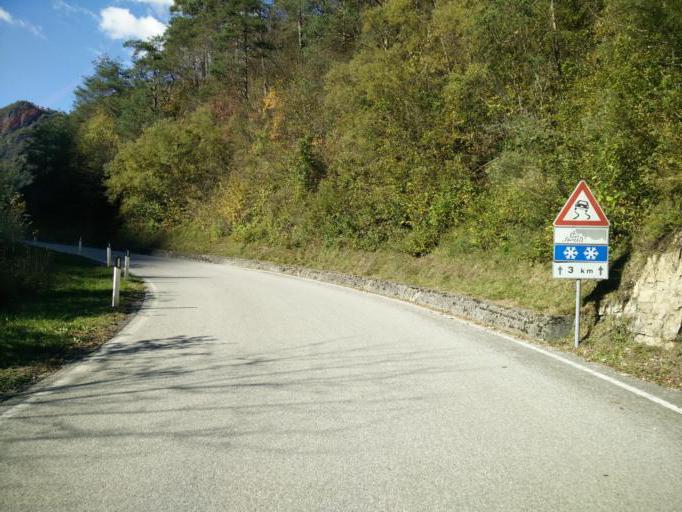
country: IT
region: Lombardy
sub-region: Provincia di Brescia
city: Valvestino
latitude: 45.7477
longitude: 10.5889
